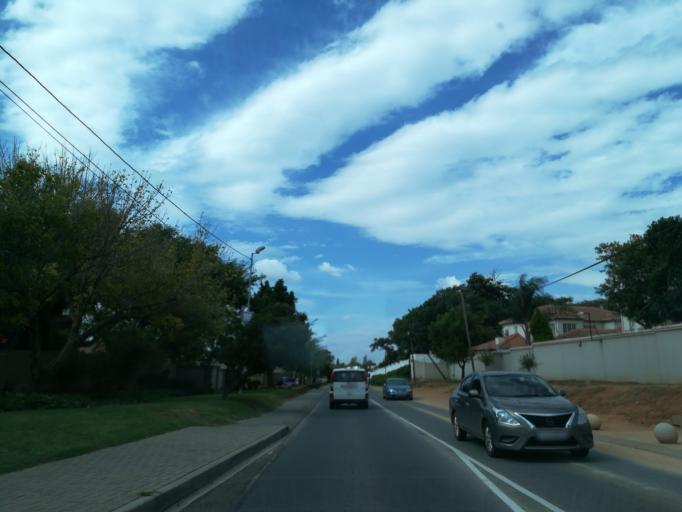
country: ZA
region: Gauteng
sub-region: West Rand District Municipality
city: Muldersdriseloop
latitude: -26.0570
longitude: 27.9608
